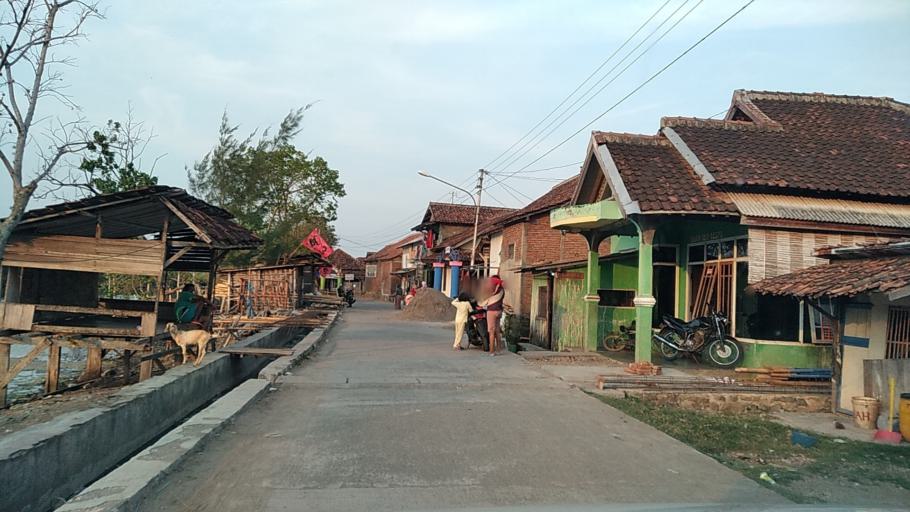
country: ID
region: Central Java
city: Semarang
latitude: -6.9541
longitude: 110.3167
